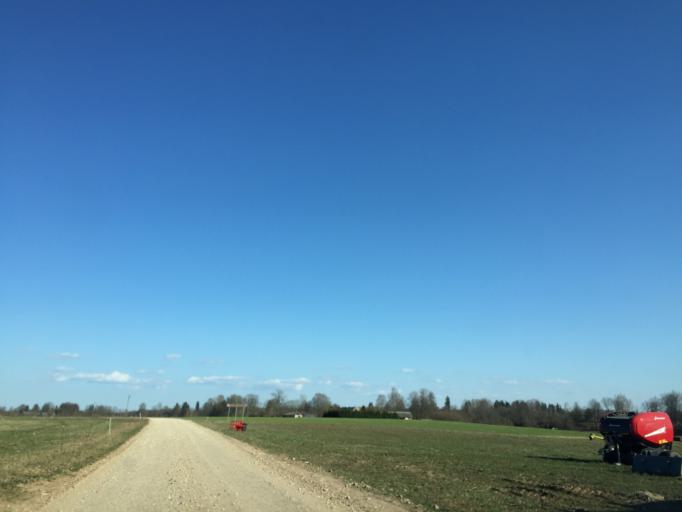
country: EE
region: Valgamaa
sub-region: Torva linn
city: Torva
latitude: 58.2393
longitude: 25.8995
